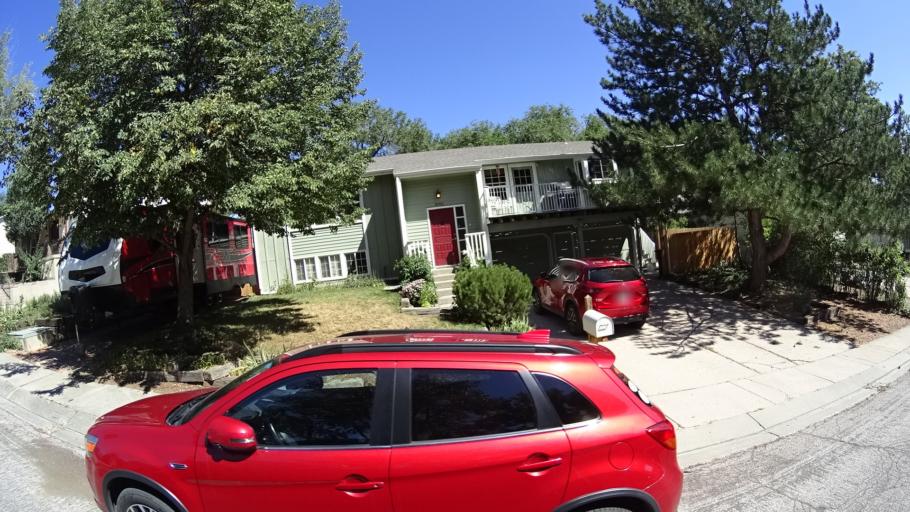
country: US
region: Colorado
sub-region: El Paso County
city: Colorado Springs
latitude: 38.8624
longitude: -104.8597
